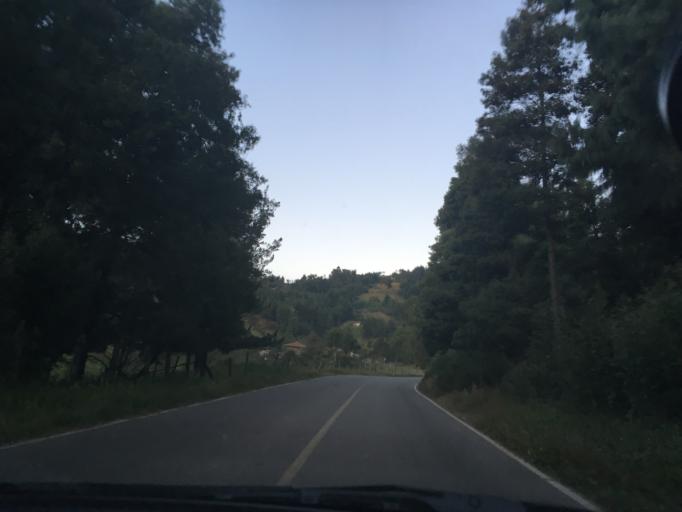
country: CO
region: Boyaca
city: Aquitania
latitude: 5.6081
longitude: -72.9089
